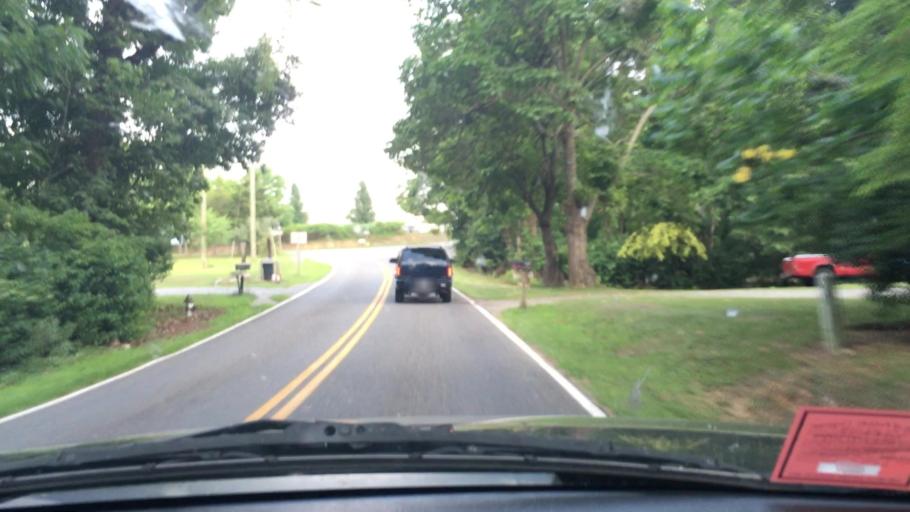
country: US
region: Virginia
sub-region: Pulaski County
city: Dublin
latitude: 37.0544
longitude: -80.6967
